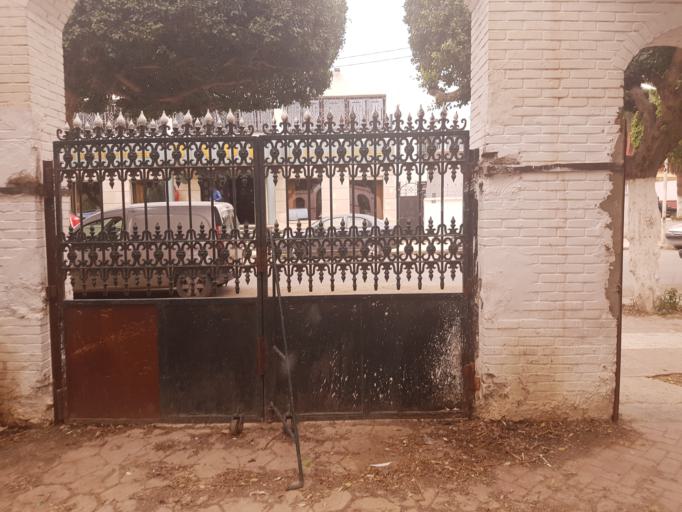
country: DZ
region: Mascara
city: Mascara
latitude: 35.5903
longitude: 0.0653
